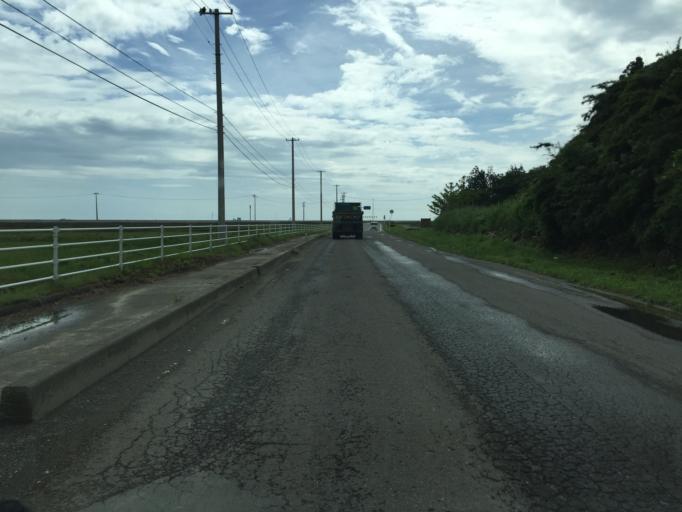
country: JP
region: Miyagi
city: Marumori
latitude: 37.7681
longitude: 140.9794
